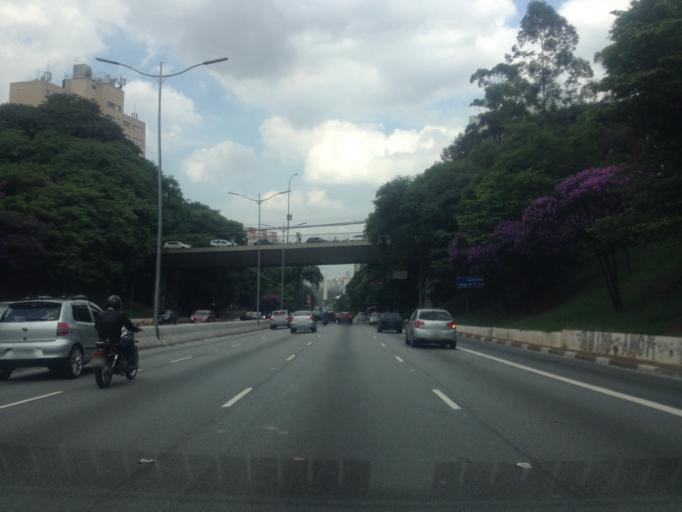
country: BR
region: Sao Paulo
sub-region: Sao Paulo
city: Sao Paulo
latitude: -23.5759
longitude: -46.6426
